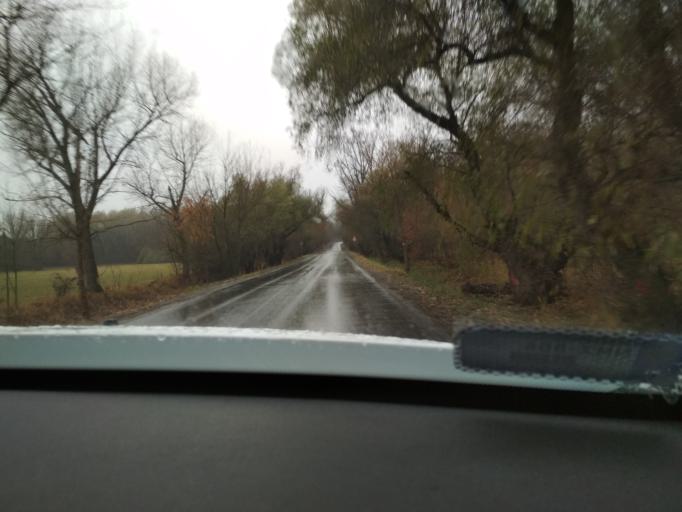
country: HU
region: Csongrad
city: Opusztaszer
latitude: 46.4399
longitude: 20.1240
